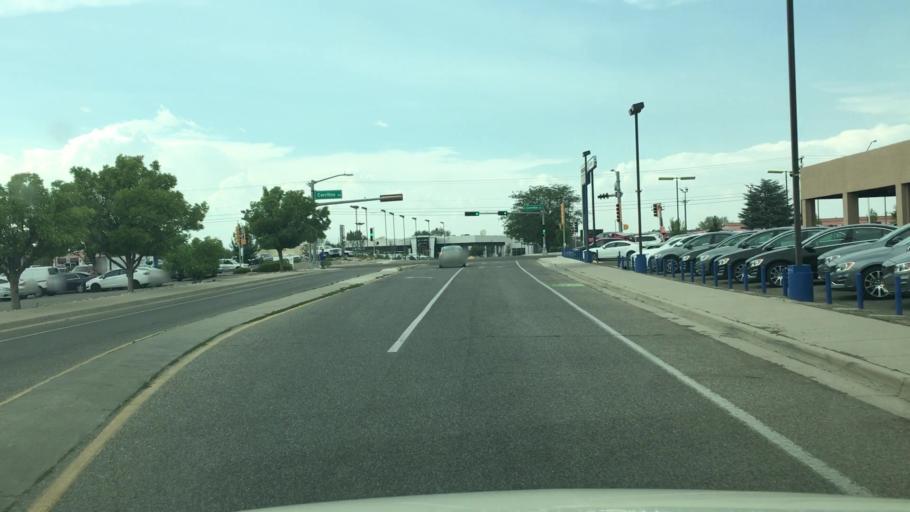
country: US
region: New Mexico
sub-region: Santa Fe County
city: Agua Fria
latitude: 35.6573
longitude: -105.9856
